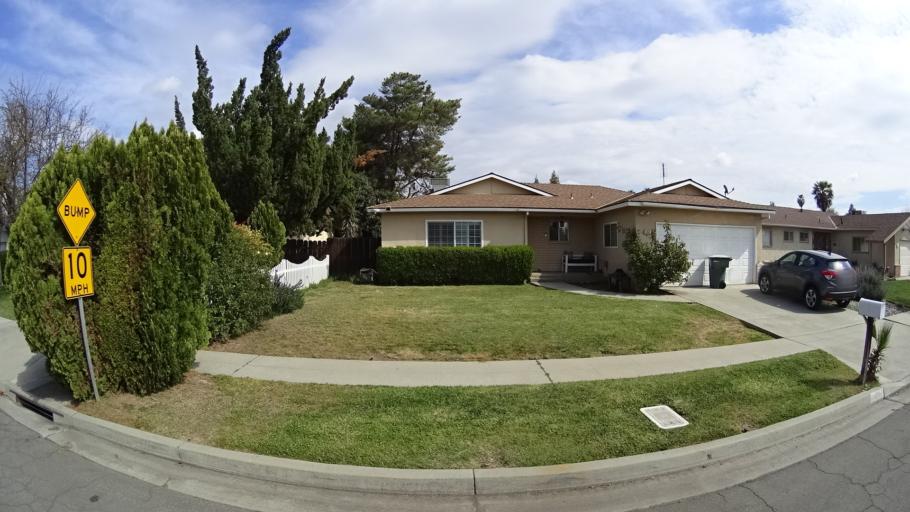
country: US
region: California
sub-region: Fresno County
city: Fresno
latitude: 36.8143
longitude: -119.8496
